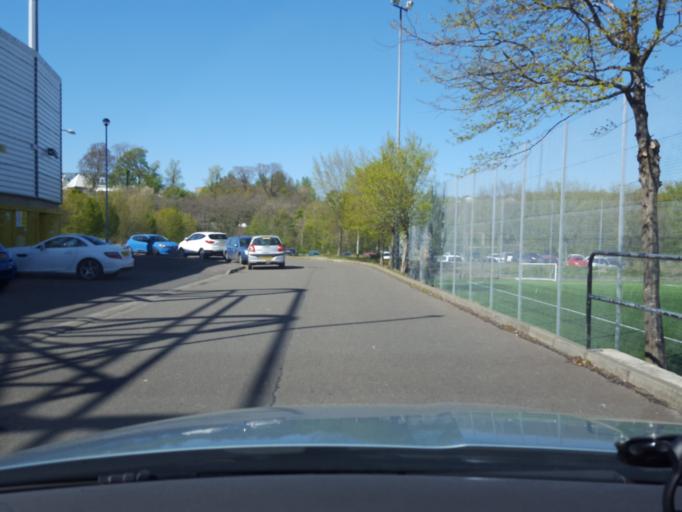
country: GB
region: Scotland
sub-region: West Lothian
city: Livingston
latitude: 55.8862
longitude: -3.5208
